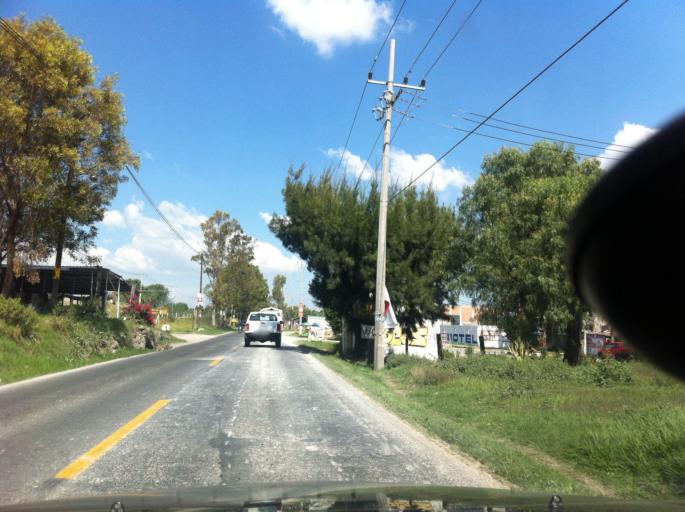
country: MX
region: Mexico
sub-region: Cuautitlan
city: La Providencia
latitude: 19.7647
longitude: -99.1245
